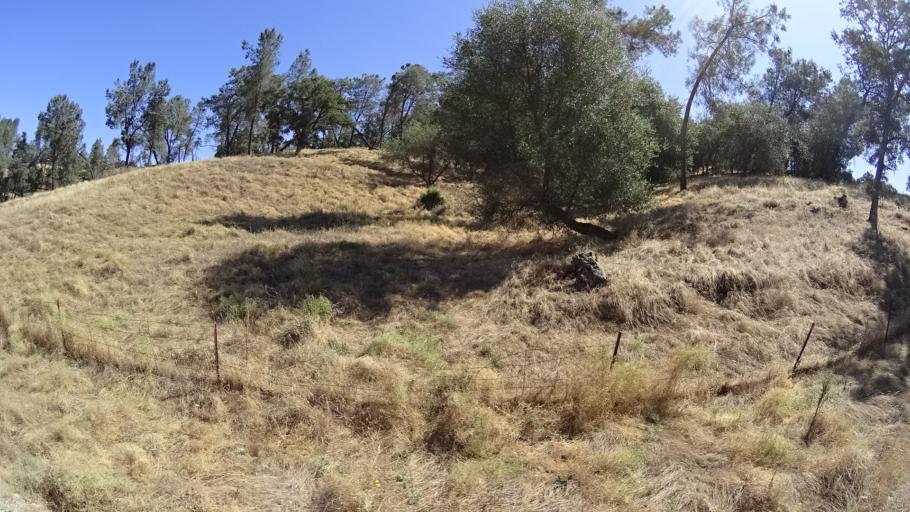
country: US
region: California
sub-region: Calaveras County
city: Valley Springs
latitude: 38.2182
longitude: -120.8754
